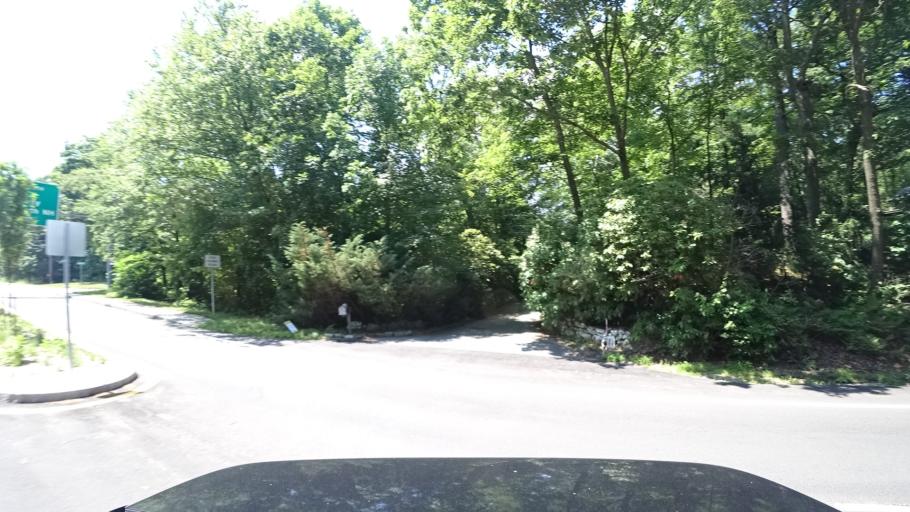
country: US
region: Massachusetts
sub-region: Norfolk County
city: Dedham
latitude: 42.2461
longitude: -71.1970
